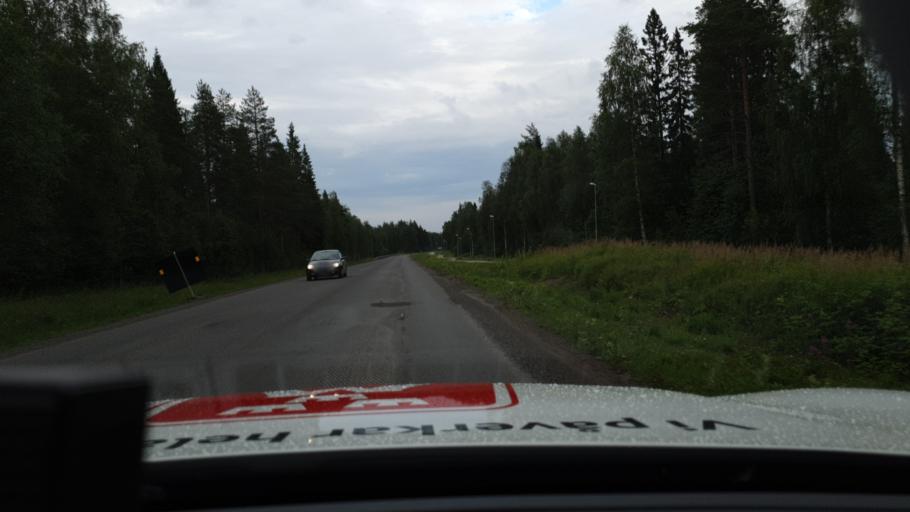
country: SE
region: Norrbotten
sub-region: Bodens Kommun
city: Boden
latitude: 65.8289
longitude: 21.6396
